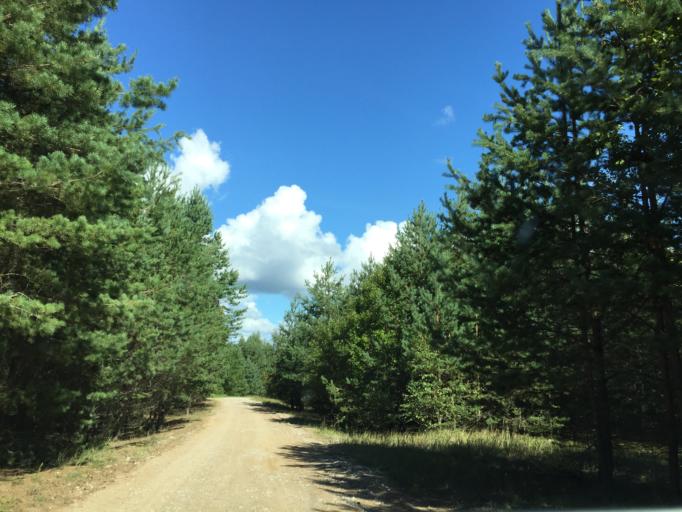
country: LV
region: Kuldigas Rajons
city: Kuldiga
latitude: 56.9727
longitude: 21.9072
